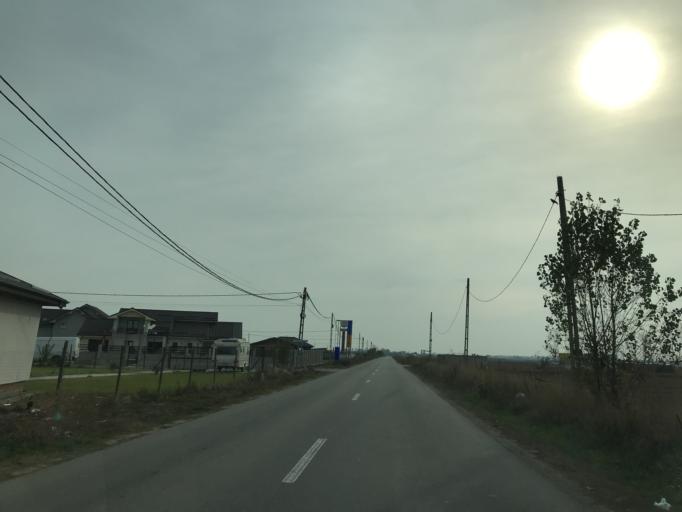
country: RO
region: Olt
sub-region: Comuna Slatioara
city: Slatioara
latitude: 44.3932
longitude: 24.3237
